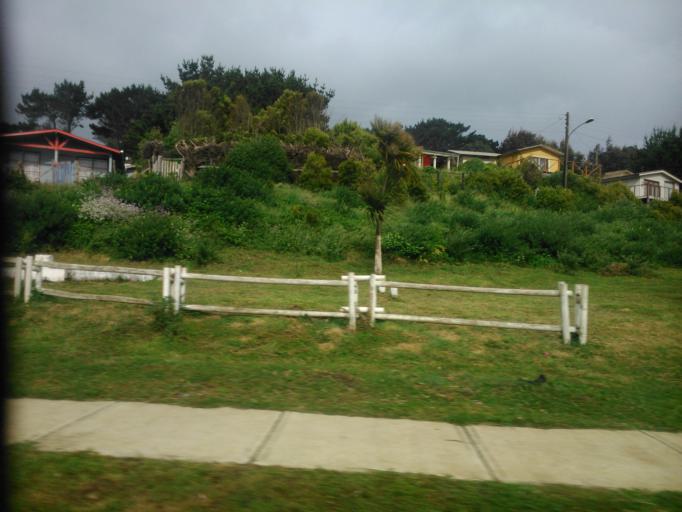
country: CL
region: Araucania
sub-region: Provincia de Cautin
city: Carahue
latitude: -38.8117
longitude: -73.3989
